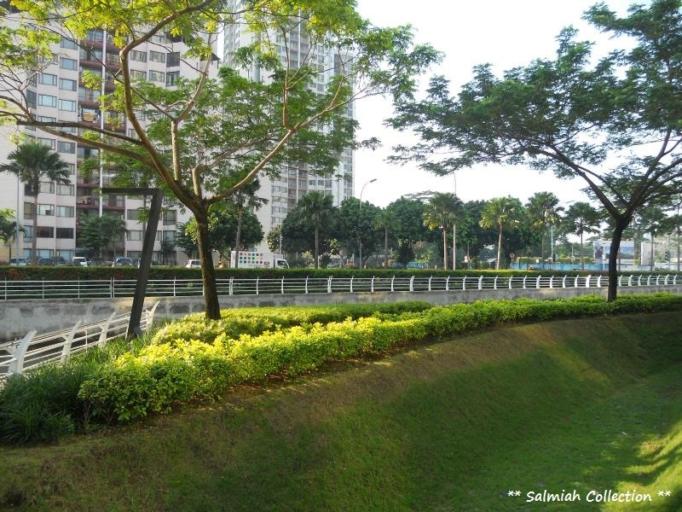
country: ID
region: Jakarta Raya
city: Jakarta
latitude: -6.2182
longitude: 106.8359
